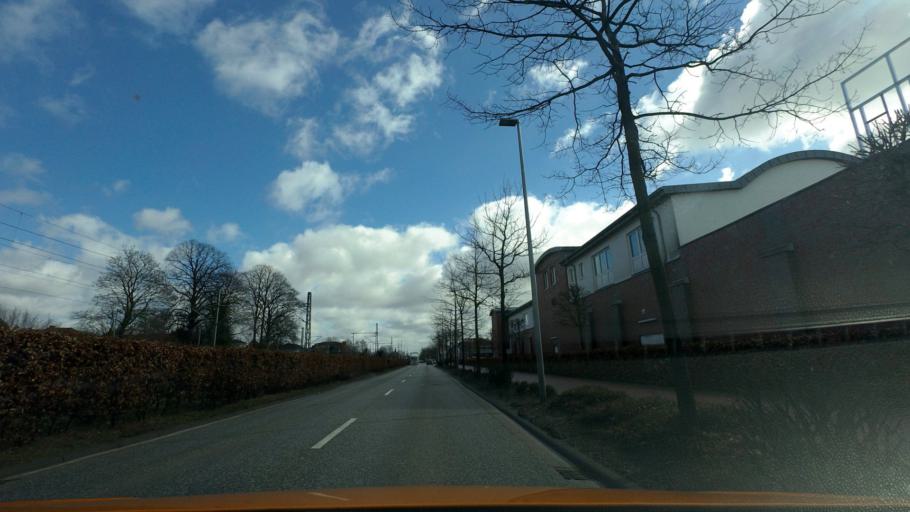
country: DE
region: Lower Saxony
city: Bad Zwischenahn
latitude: 53.1821
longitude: 8.0046
